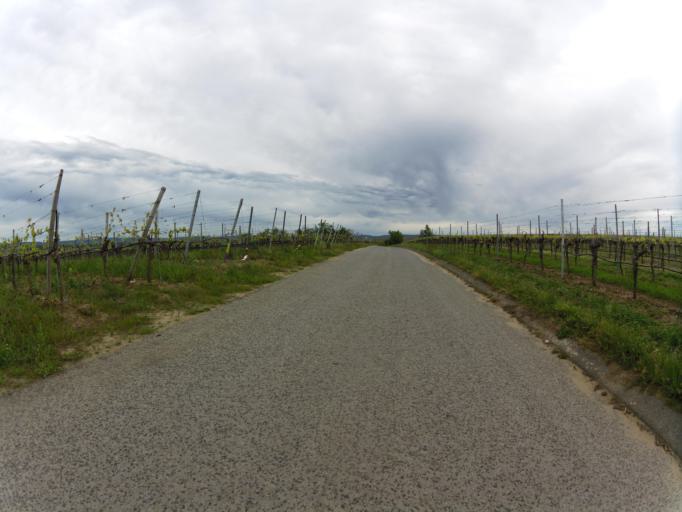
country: DE
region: Bavaria
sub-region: Regierungsbezirk Unterfranken
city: Sommerach
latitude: 49.8493
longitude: 10.1992
